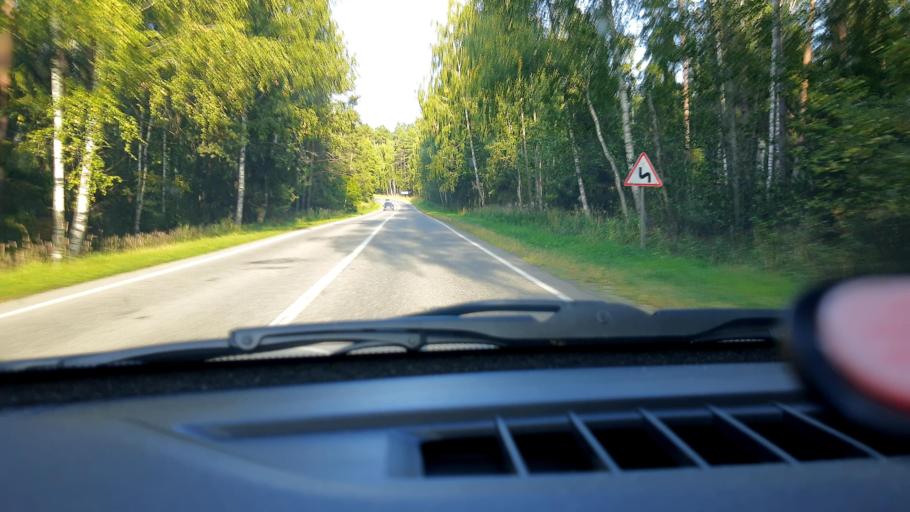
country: RU
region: Nizjnij Novgorod
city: Gorodets
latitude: 56.6633
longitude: 43.5830
